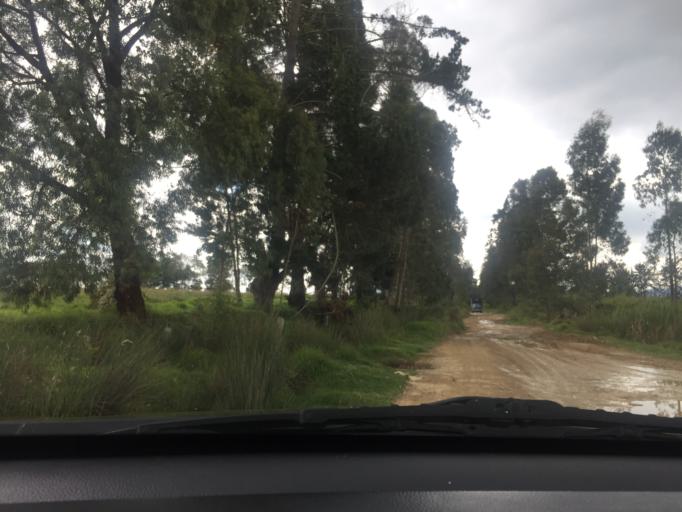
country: CO
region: Cundinamarca
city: Madrid
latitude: 4.7866
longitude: -74.2811
